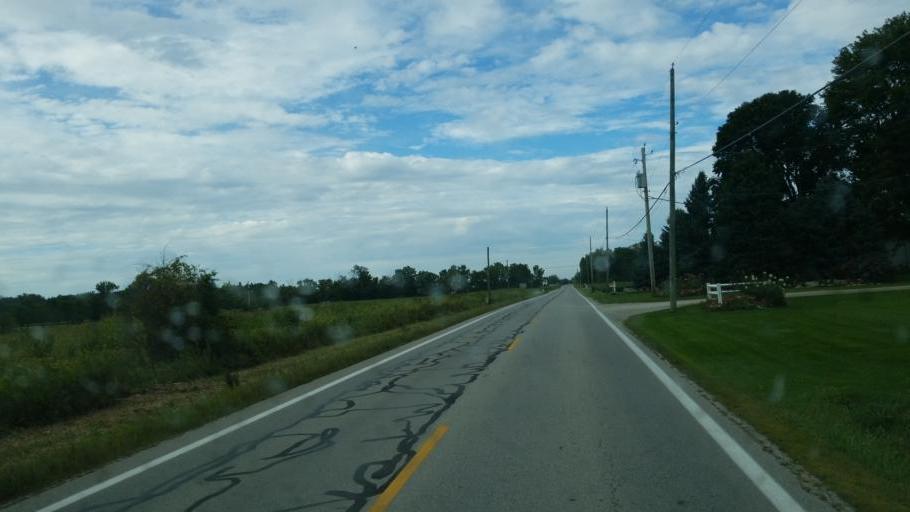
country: US
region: Ohio
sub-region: Delaware County
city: Sunbury
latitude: 40.1843
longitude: -82.8061
